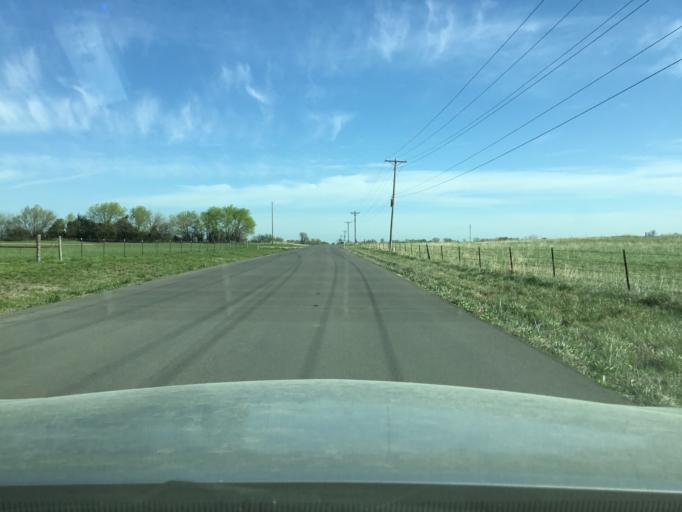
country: US
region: Kansas
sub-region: Neosho County
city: Chanute
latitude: 37.6479
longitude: -95.4435
